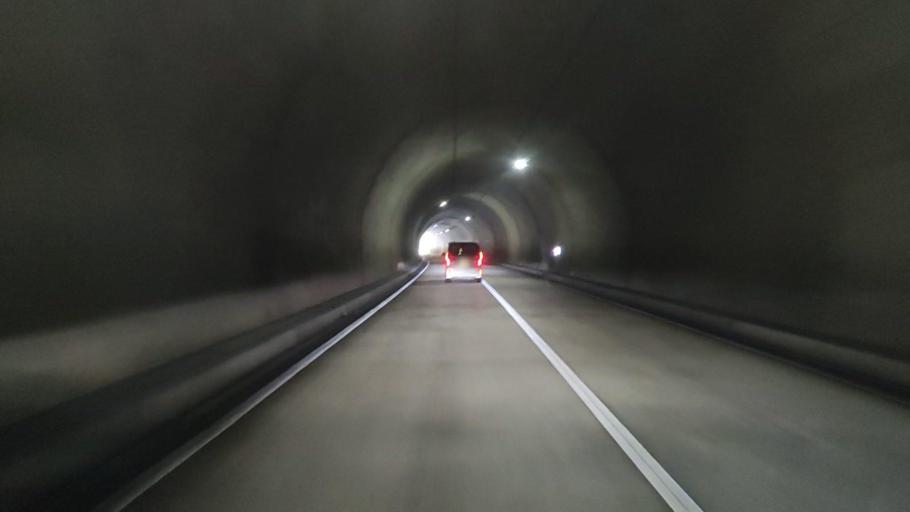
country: JP
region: Wakayama
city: Shingu
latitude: 33.8868
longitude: 135.8795
